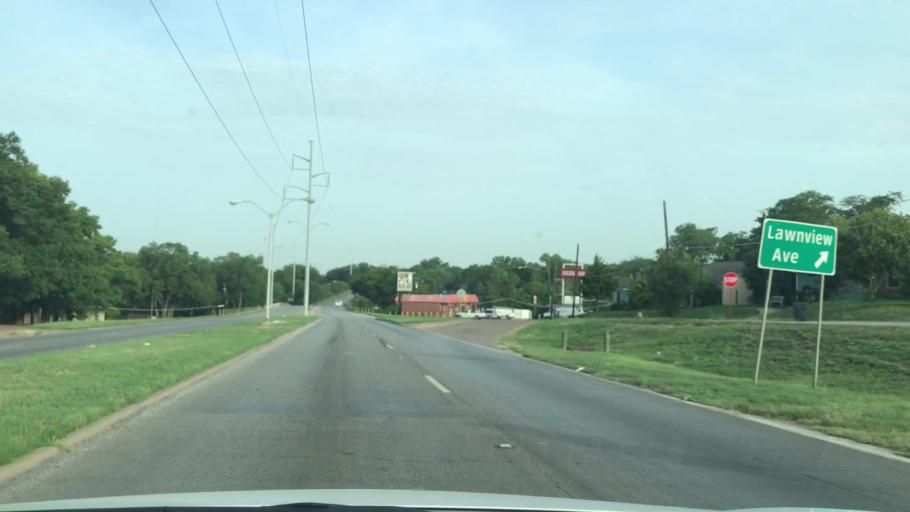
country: US
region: Texas
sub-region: Dallas County
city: Dallas
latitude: 32.7765
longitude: -96.7156
